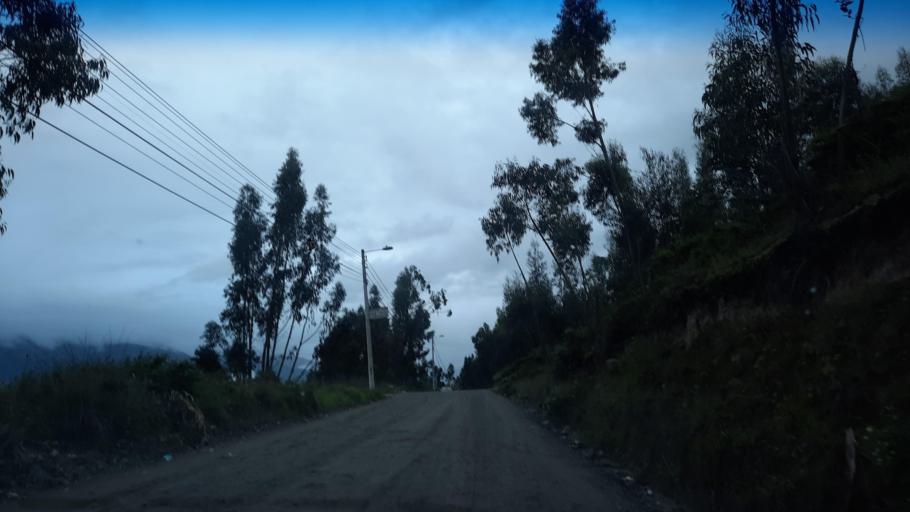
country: EC
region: Chimborazo
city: Riobamba
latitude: -1.6850
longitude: -78.6594
